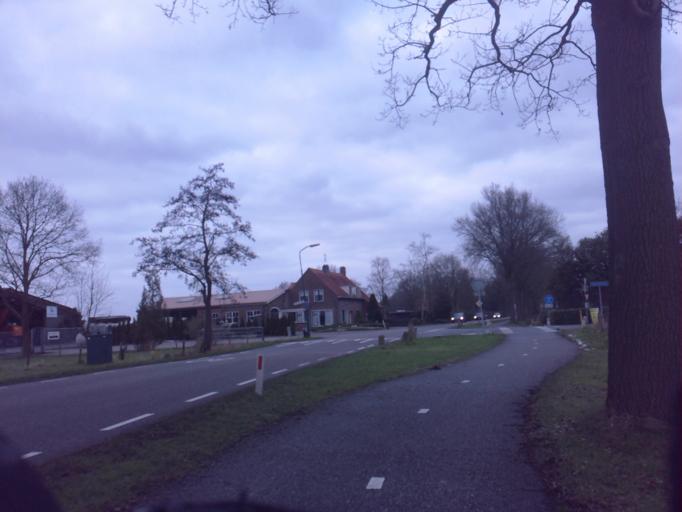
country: NL
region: Utrecht
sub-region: Gemeente Leusden
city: Leusden
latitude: 52.1472
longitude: 5.4514
